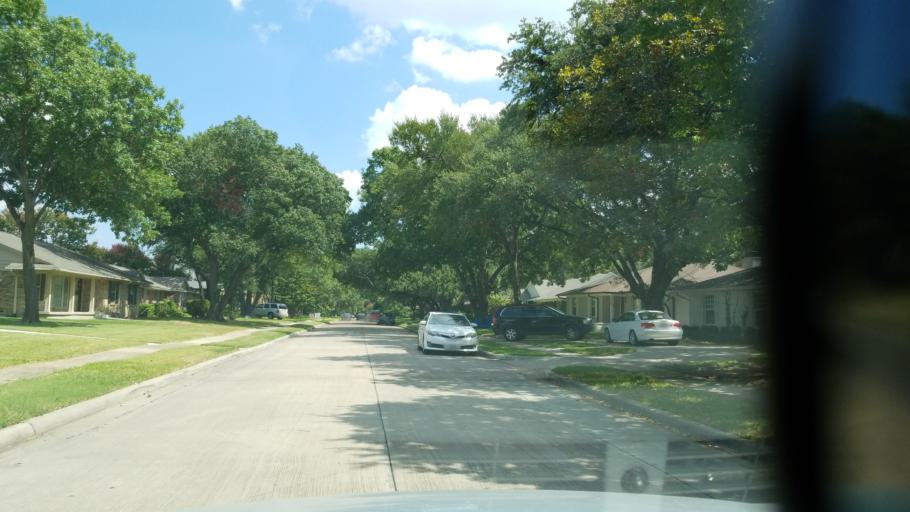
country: US
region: Texas
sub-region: Dallas County
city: Richardson
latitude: 32.9672
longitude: -96.7666
